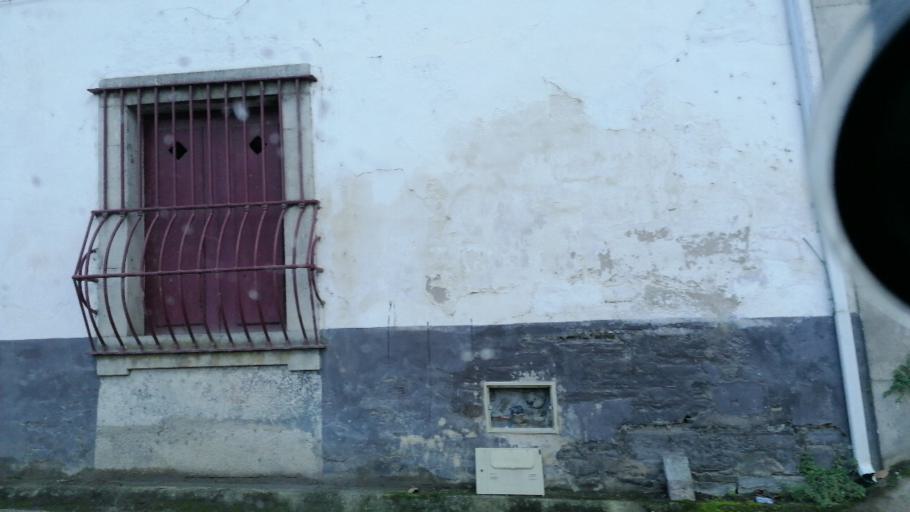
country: PT
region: Vila Real
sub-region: Peso da Regua
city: Peso da Regua
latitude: 41.1502
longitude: -7.7841
